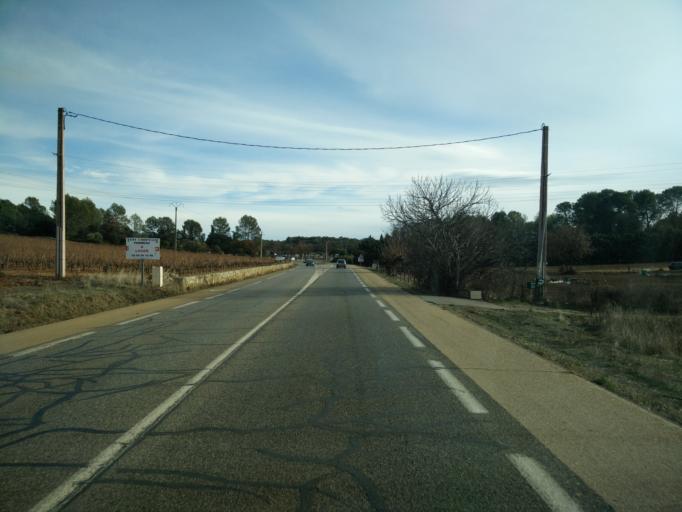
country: FR
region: Provence-Alpes-Cote d'Azur
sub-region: Departement du Var
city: Lorgues
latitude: 43.4683
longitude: 6.3851
